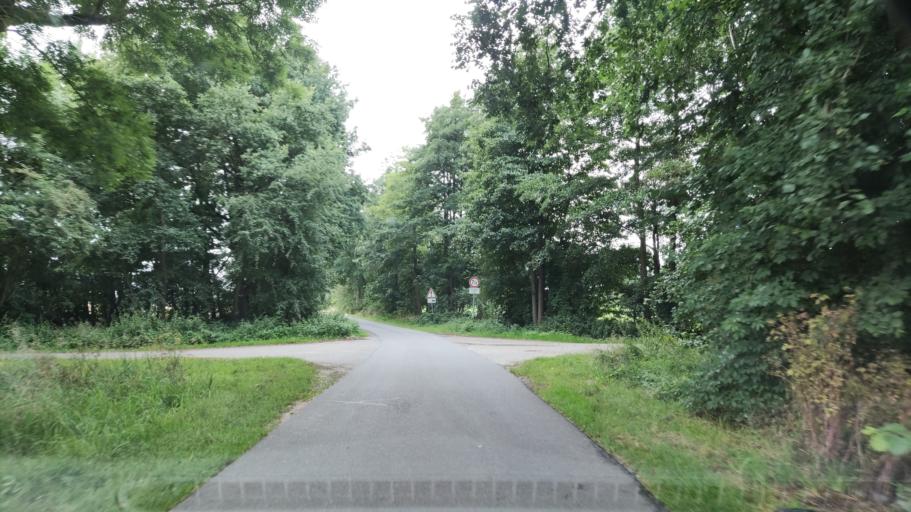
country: DE
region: Lower Saxony
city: Klein Gusborn
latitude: 53.0909
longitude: 11.1423
